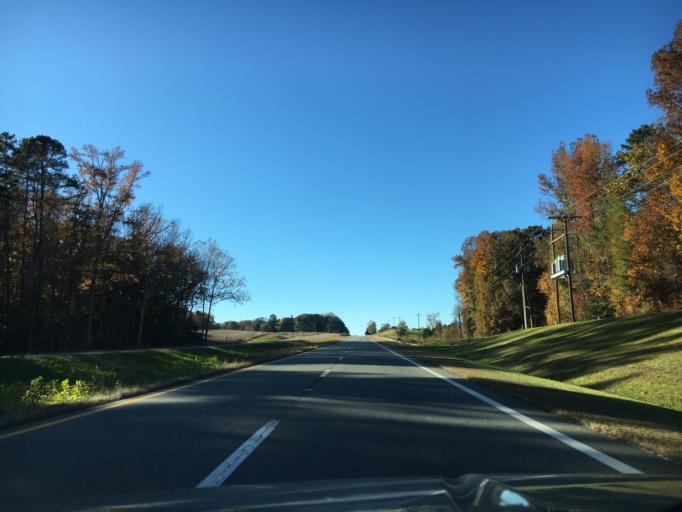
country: US
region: Virginia
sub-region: Halifax County
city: South Boston
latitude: 36.6780
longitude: -78.8304
